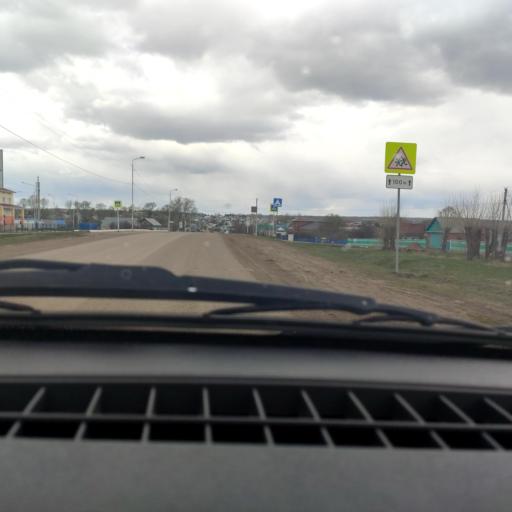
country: RU
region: Bashkortostan
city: Chekmagush
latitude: 55.1322
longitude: 54.6767
